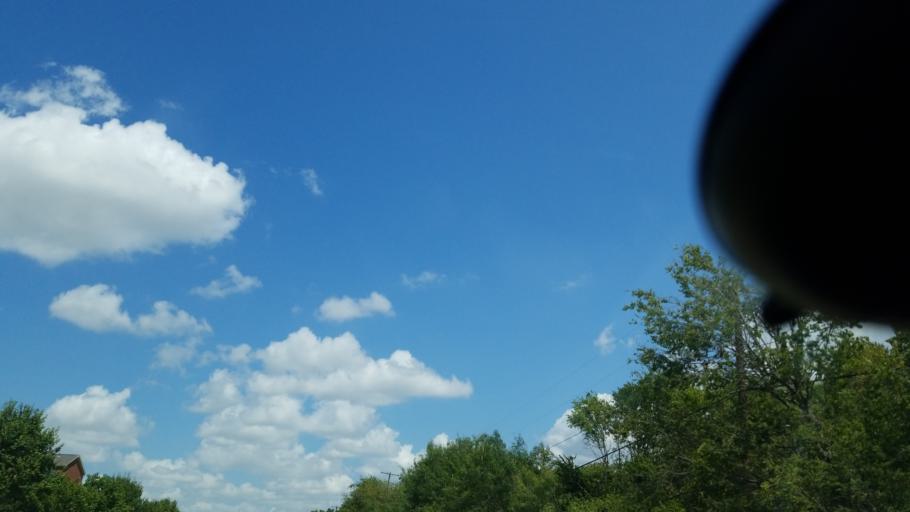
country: US
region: Texas
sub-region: Dallas County
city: Grand Prairie
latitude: 32.7326
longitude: -96.9858
